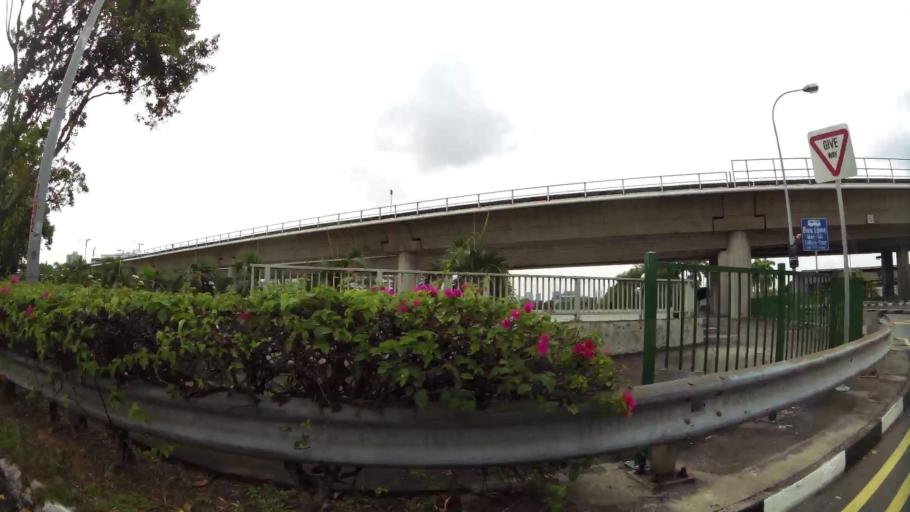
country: MY
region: Johor
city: Johor Bahru
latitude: 1.4361
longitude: 103.7850
